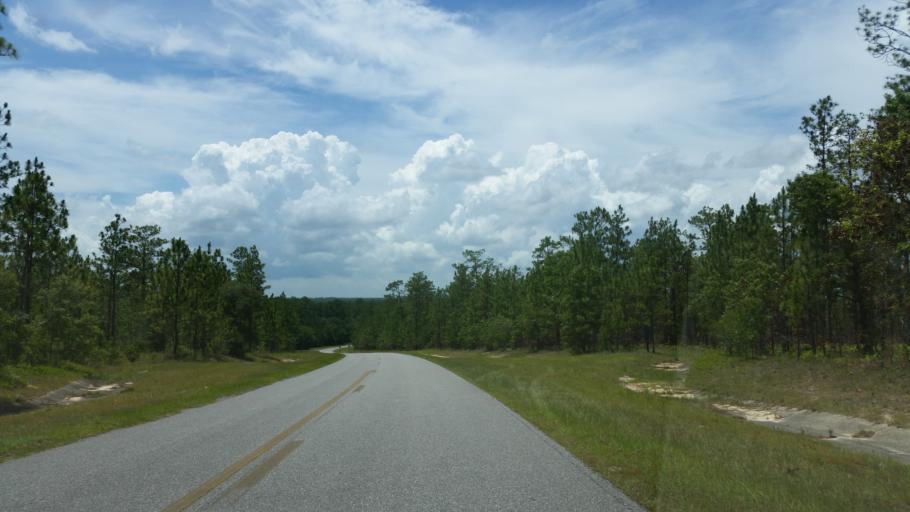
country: US
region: Florida
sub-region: Okaloosa County
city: Crestview
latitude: 30.7187
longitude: -86.7828
